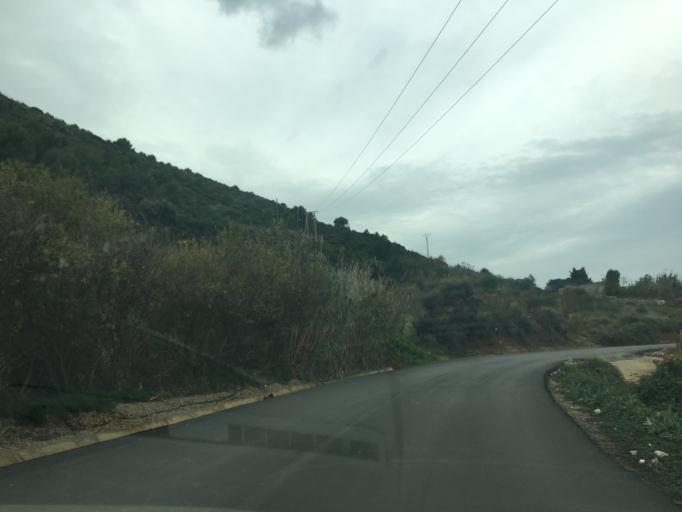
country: DZ
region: Tipaza
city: Tipasa
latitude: 36.6362
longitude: 2.3116
